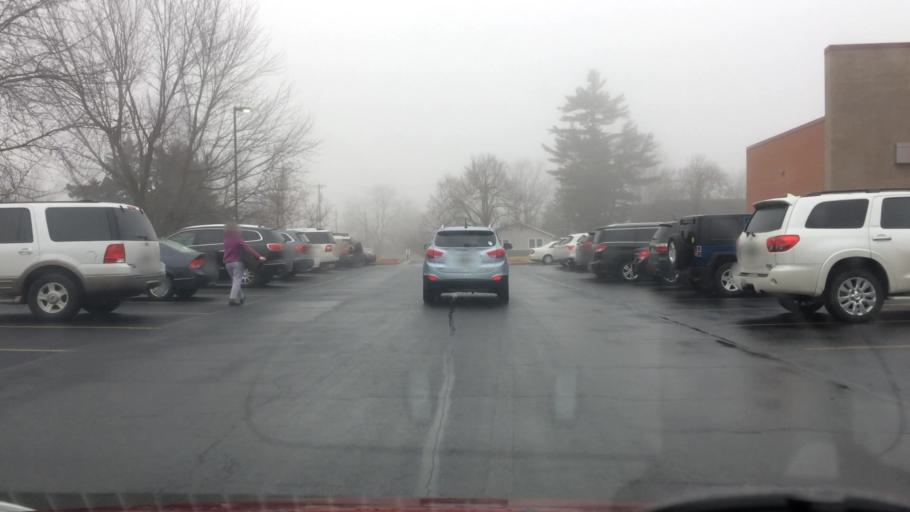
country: US
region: Missouri
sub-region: Greene County
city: Strafford
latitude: 37.2699
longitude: -93.1216
